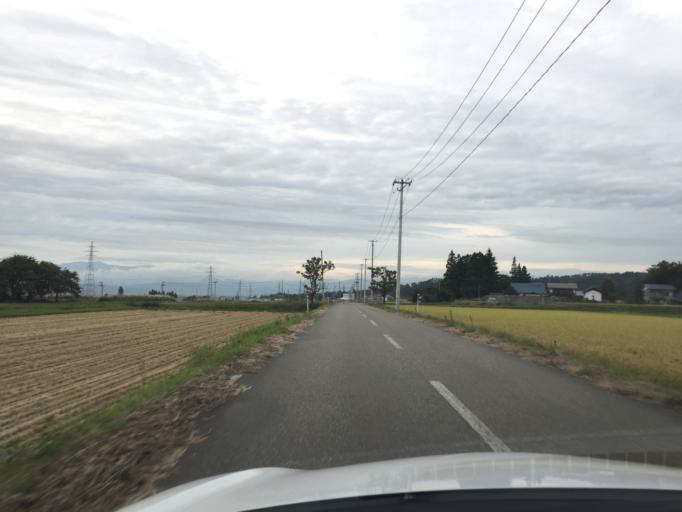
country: JP
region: Fukushima
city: Kitakata
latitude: 37.5667
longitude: 139.9278
